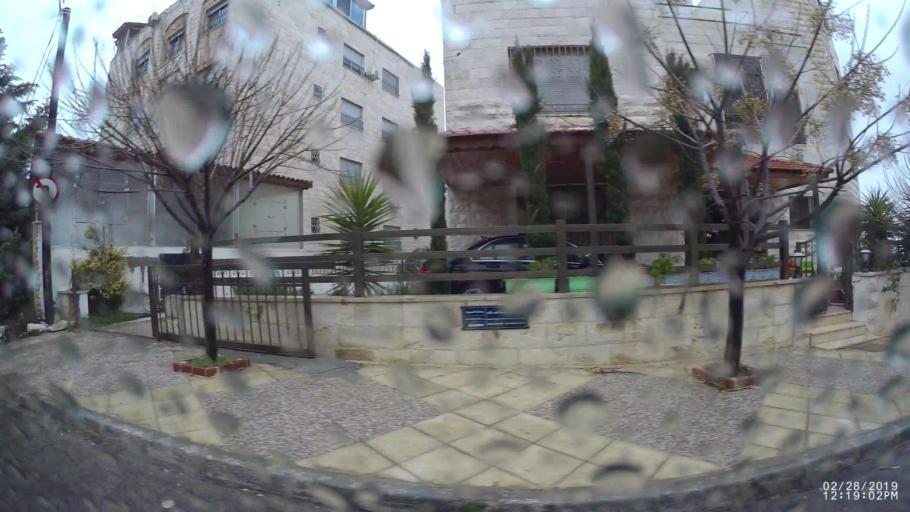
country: JO
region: Amman
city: Al Jubayhah
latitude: 32.0263
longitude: 35.8864
